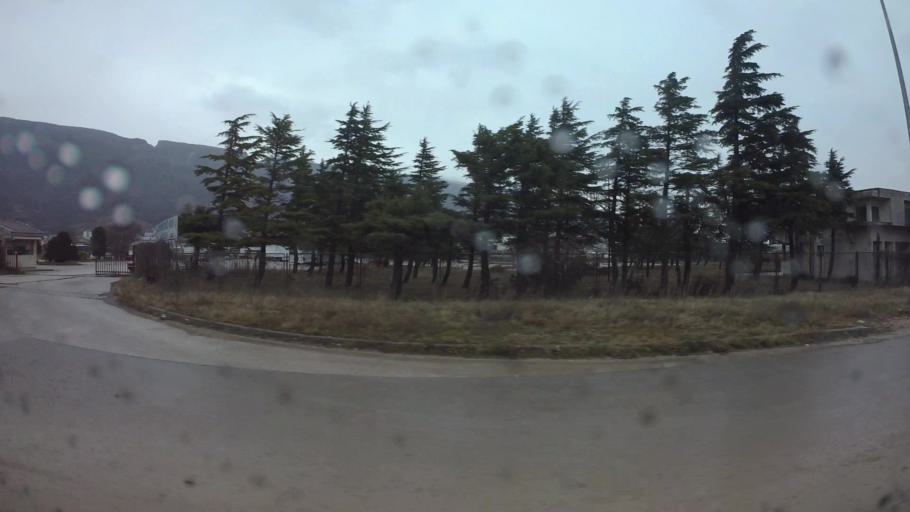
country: BA
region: Federation of Bosnia and Herzegovina
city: Rodoc
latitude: 43.3168
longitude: 17.8295
